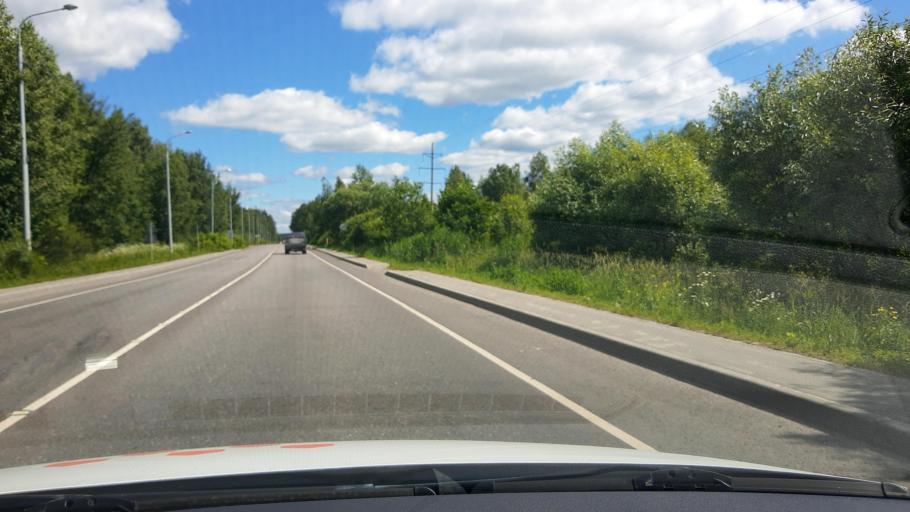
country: RU
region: Moskovskaya
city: Noginsk
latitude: 55.8563
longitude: 38.4055
